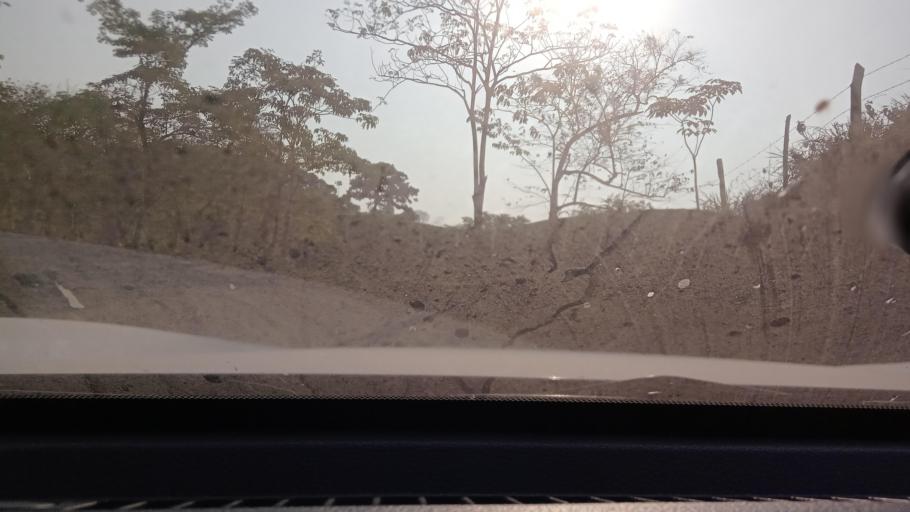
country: MX
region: Tabasco
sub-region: Huimanguillo
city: Francisco Rueda
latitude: 17.6639
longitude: -93.8628
